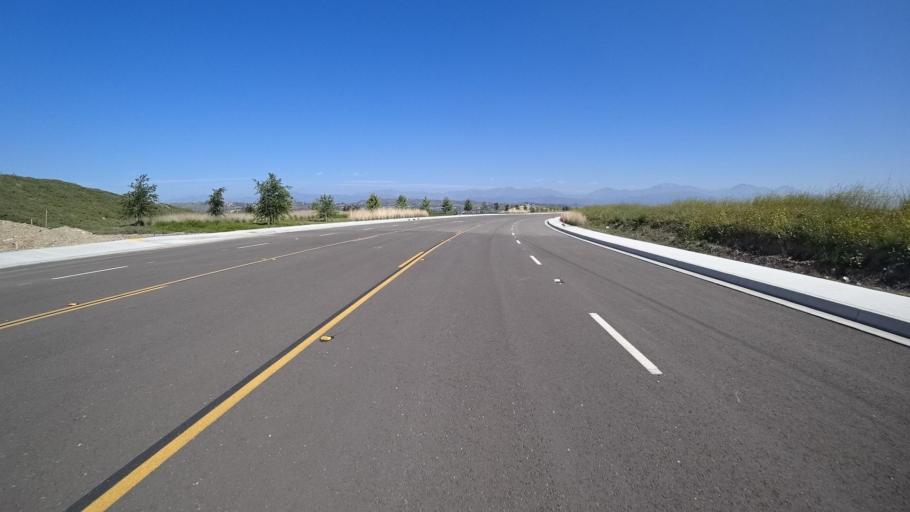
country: US
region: California
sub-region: Los Angeles County
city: Diamond Bar
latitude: 34.0063
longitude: -117.8340
